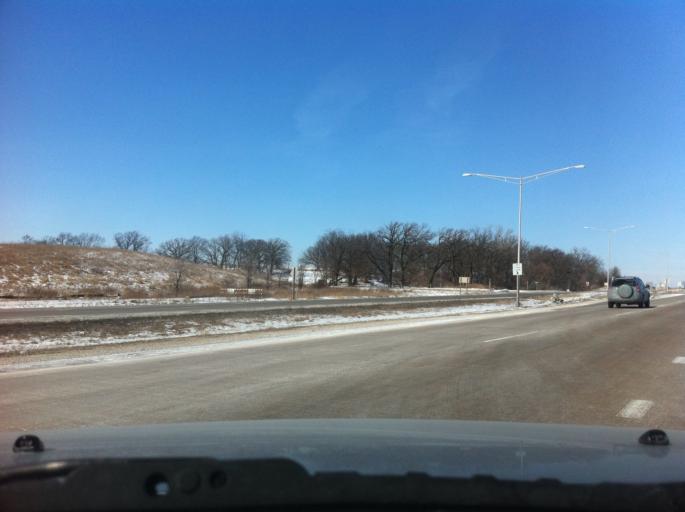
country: US
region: Wisconsin
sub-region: Dane County
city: Windsor
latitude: 43.1849
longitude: -89.3239
